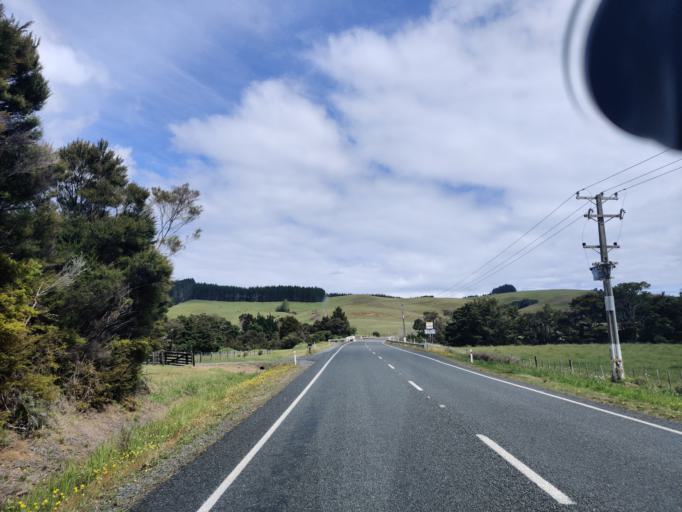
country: NZ
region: Northland
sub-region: Far North District
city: Taipa
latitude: -35.0157
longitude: 173.6262
